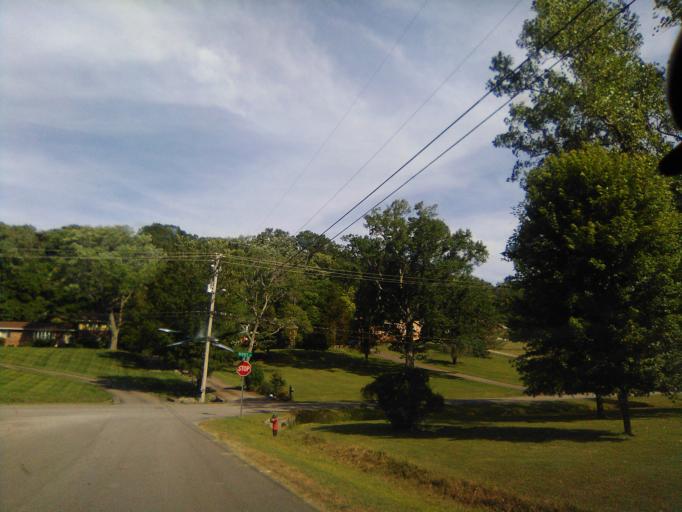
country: US
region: Tennessee
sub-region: Davidson County
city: Belle Meade
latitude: 36.1098
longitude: -86.9095
